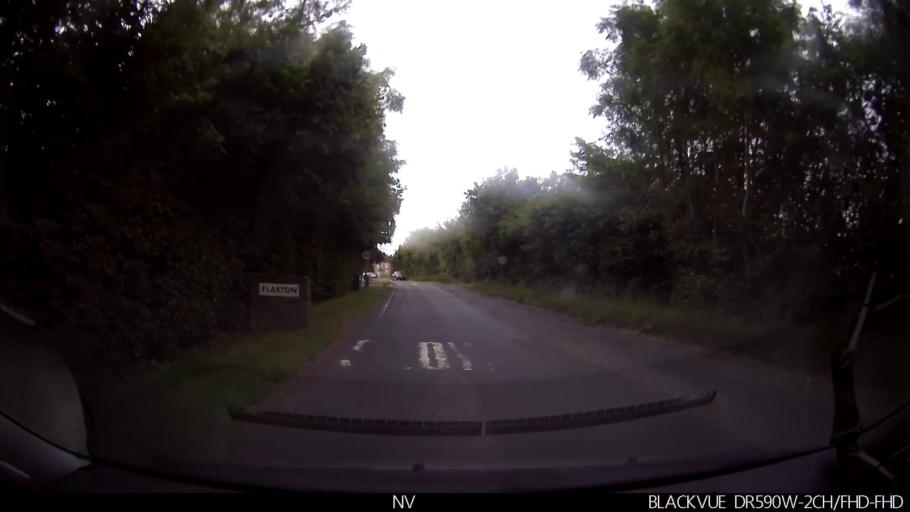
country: GB
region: England
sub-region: City of York
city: Holtby
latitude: 54.0480
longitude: -0.9591
